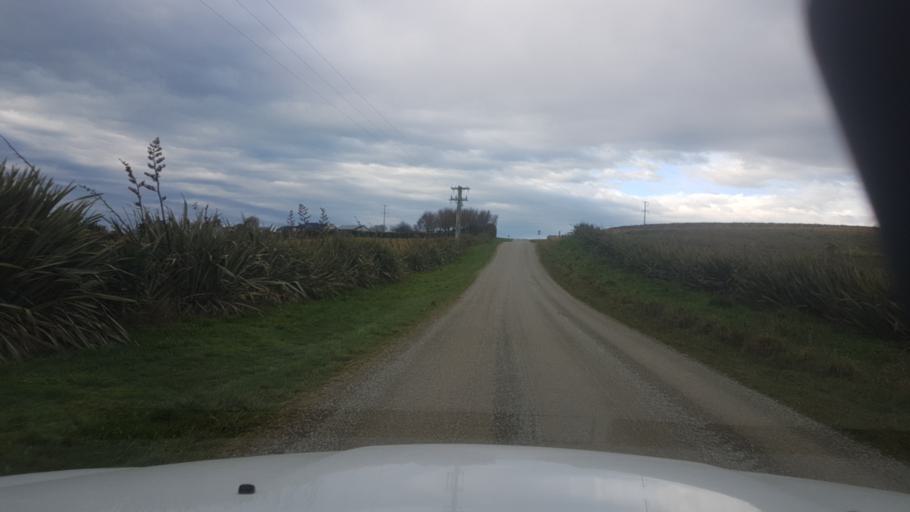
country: NZ
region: Canterbury
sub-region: Timaru District
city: Pleasant Point
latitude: -44.3525
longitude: 171.1556
